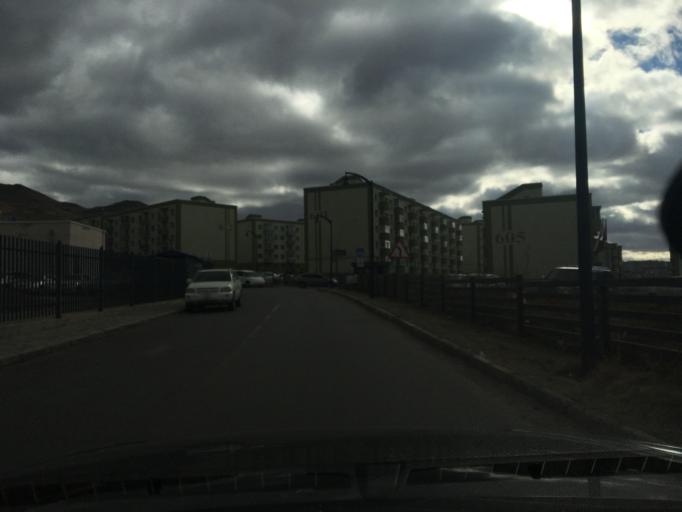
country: MN
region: Ulaanbaatar
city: Ulaanbaatar
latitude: 47.8795
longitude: 106.8493
